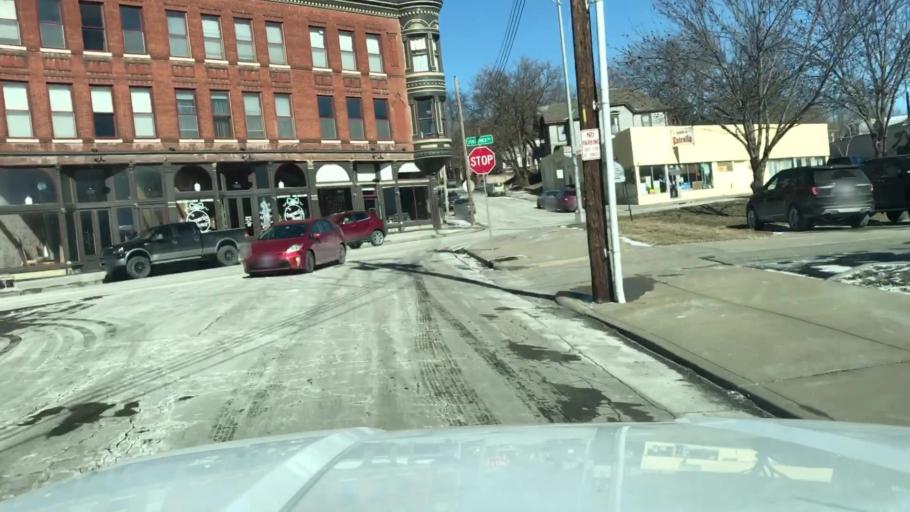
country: US
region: Missouri
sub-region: Buchanan County
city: Saint Joseph
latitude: 39.7696
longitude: -94.8454
